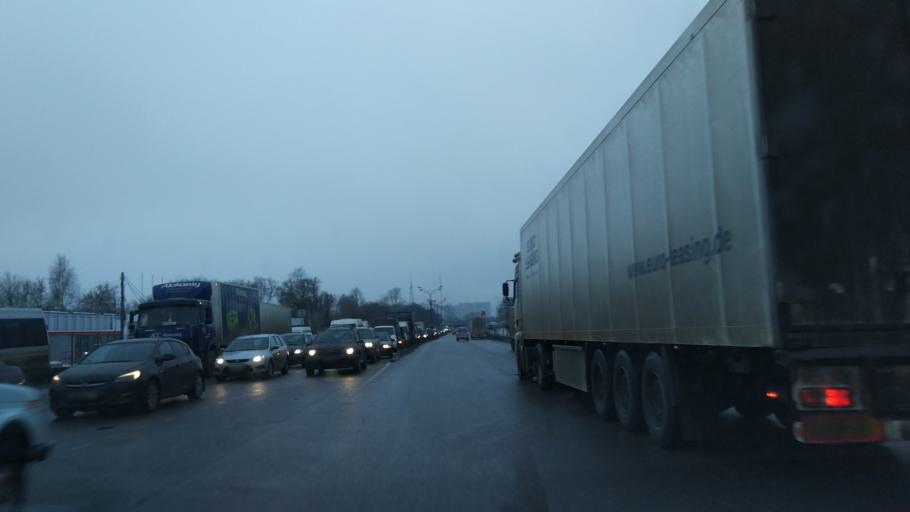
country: RU
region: Moskovskaya
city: Saltykovka
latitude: 55.7937
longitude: 37.9240
